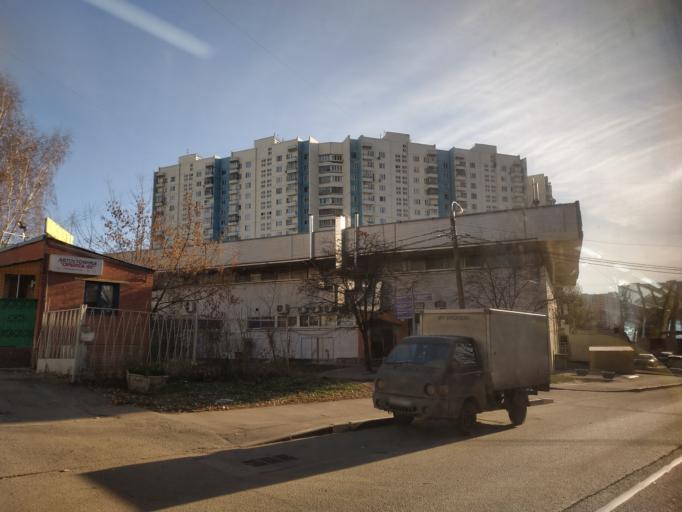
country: RU
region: Moscow
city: Biryulevo
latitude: 55.5840
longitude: 37.6822
